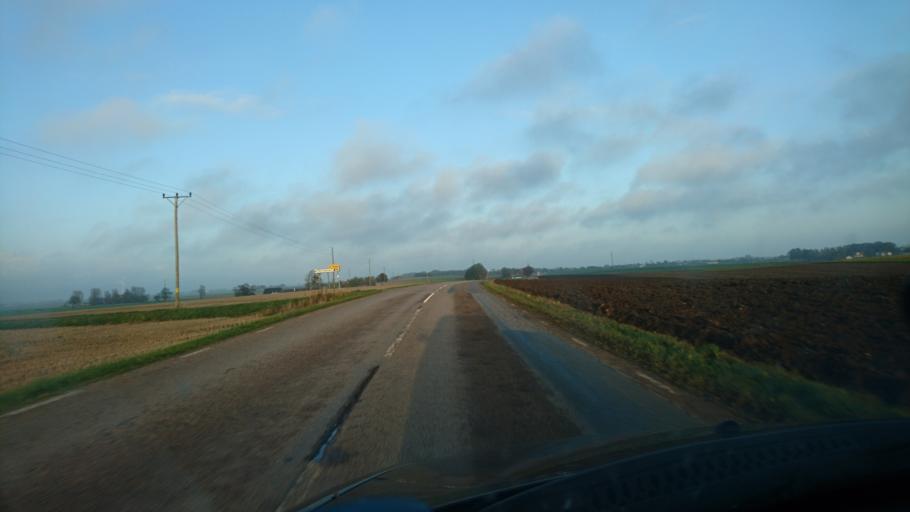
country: SE
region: Skane
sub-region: Tomelilla Kommun
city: Tomelilla
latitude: 55.4510
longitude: 14.1480
